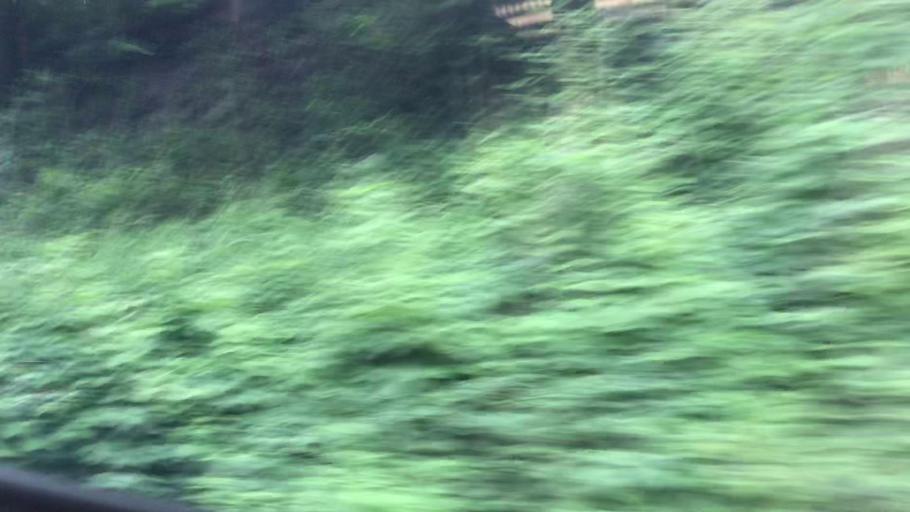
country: PL
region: Lower Silesian Voivodeship
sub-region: Powiat walbrzyski
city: Walbrzych
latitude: 50.7708
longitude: 16.2676
